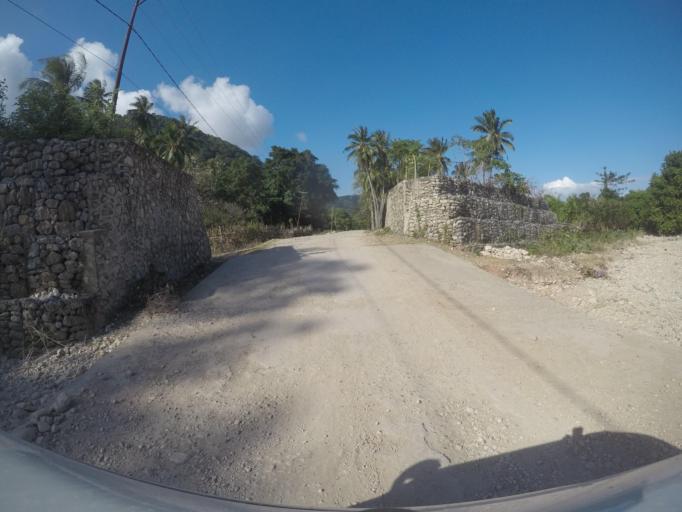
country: TL
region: Viqueque
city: Viqueque
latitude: -8.8031
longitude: 126.5837
